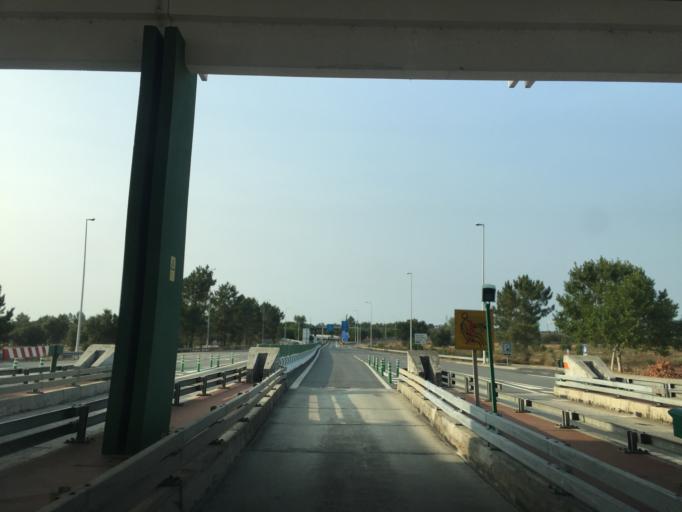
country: PT
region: Setubal
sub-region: Setubal
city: Setubal
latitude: 38.5977
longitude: -8.6736
